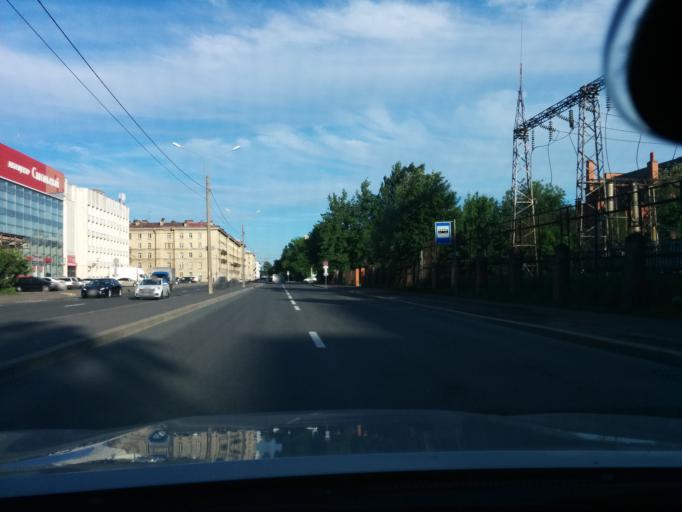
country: RU
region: Leningrad
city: Finlyandskiy
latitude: 59.9727
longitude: 30.3802
